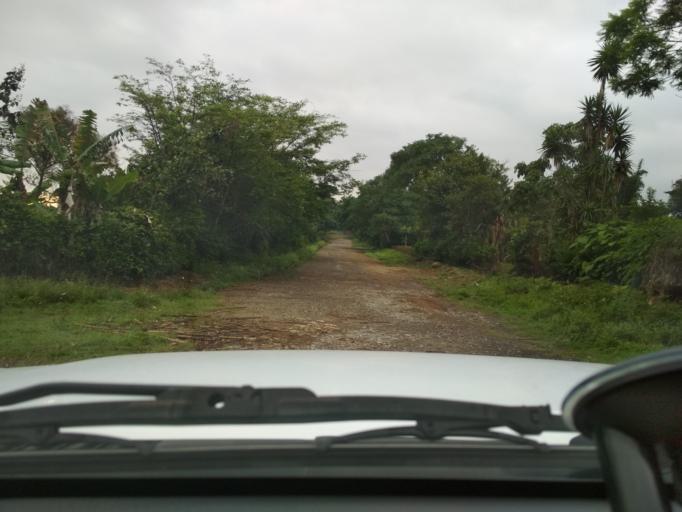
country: MX
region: Veracruz
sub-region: Fortin
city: Monte Salas
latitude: 18.9225
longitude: -97.0429
